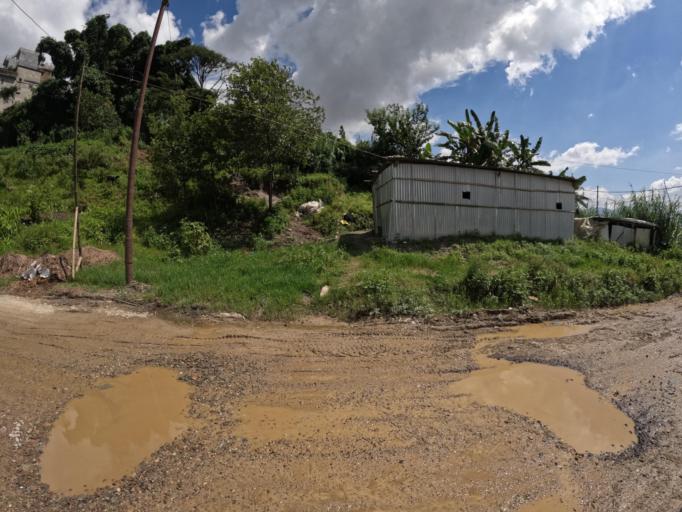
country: NP
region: Central Region
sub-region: Bagmati Zone
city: Kathmandu
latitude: 27.7701
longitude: 85.3273
